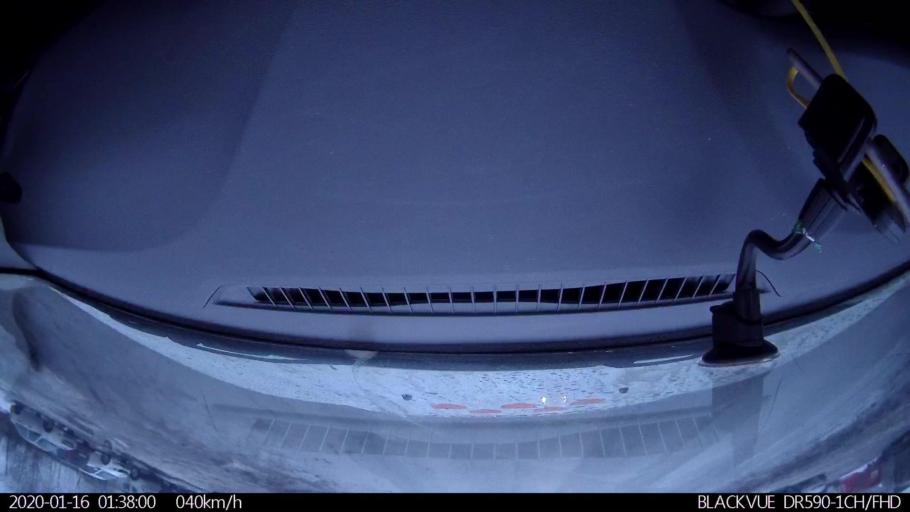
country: RU
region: Nizjnij Novgorod
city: Gorbatovka
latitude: 56.3390
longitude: 43.8042
